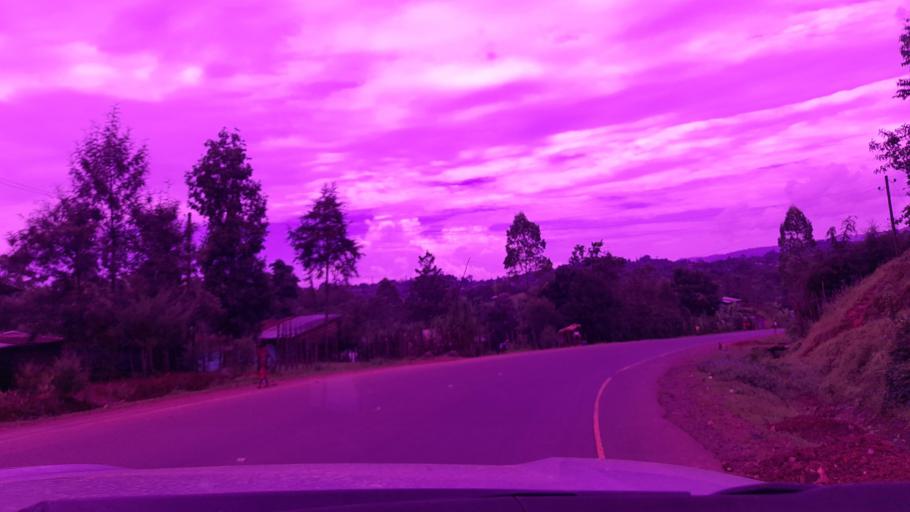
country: ET
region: Southern Nations, Nationalities, and People's Region
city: Mizan Teferi
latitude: 7.0026
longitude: 35.6029
